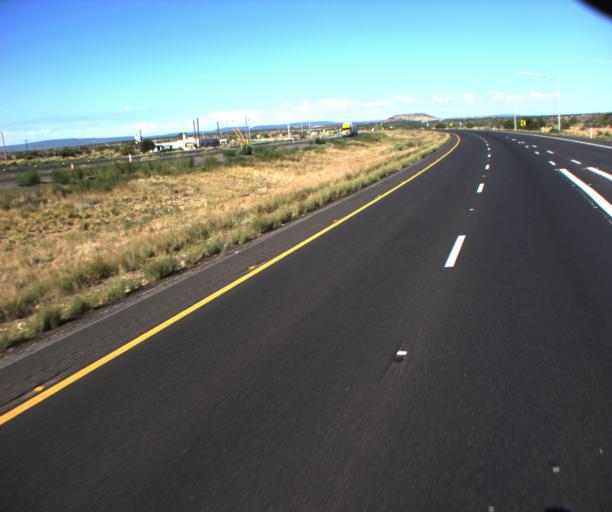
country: US
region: Arizona
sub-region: Coconino County
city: Flagstaff
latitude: 35.1622
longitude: -111.2773
